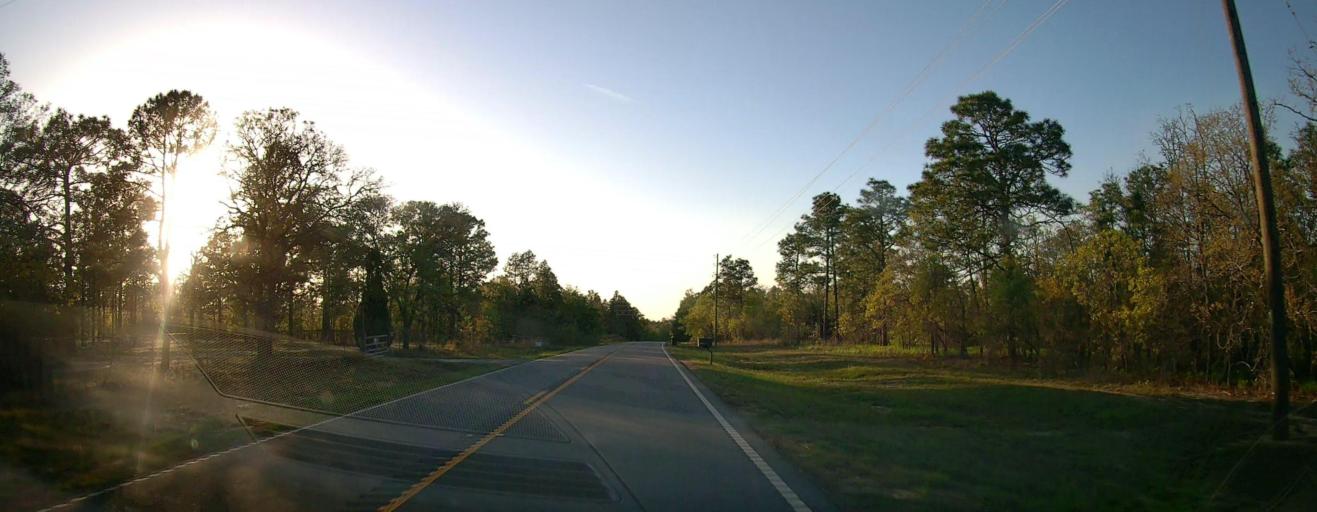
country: US
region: Georgia
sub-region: Talbot County
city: Talbotton
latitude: 32.5279
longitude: -84.4795
